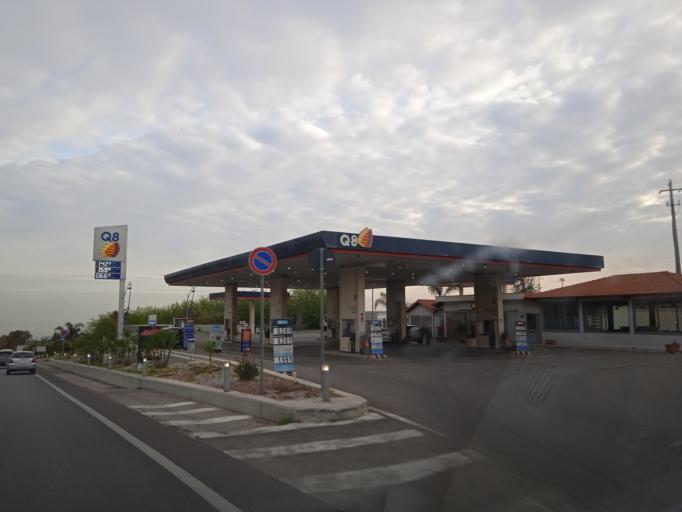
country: IT
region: Sicily
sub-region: Palermo
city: Portella di Mare
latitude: 38.0647
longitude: 13.4613
